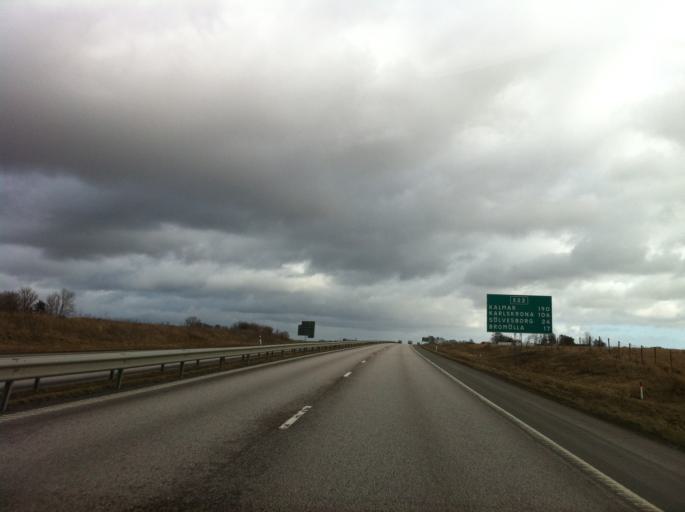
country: SE
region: Skane
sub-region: Kristianstads Kommun
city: Onnestad
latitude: 56.0294
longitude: 14.0809
